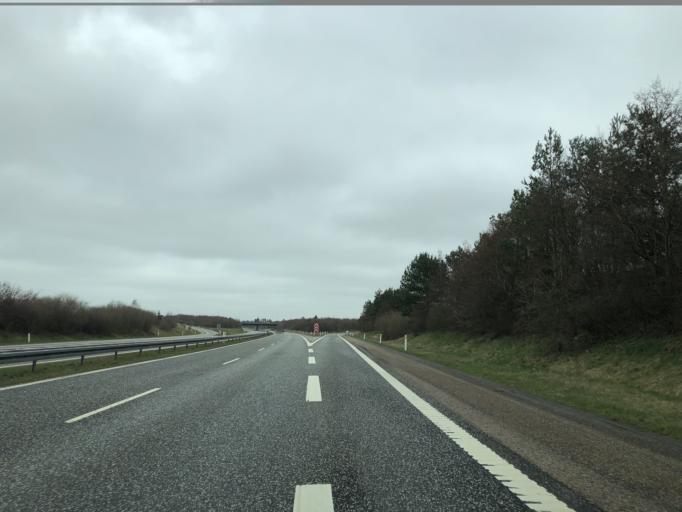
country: DK
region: North Denmark
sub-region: Frederikshavn Kommune
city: Saeby
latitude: 57.3089
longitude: 10.4454
